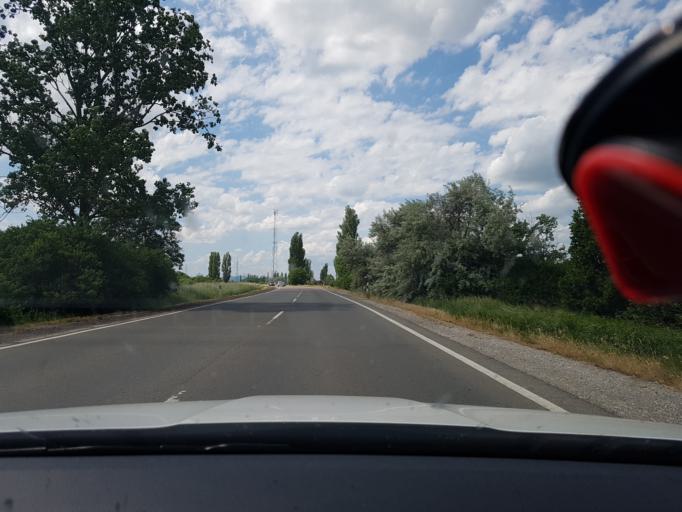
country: HU
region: Heves
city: Kompolt
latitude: 47.7634
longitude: 20.2251
